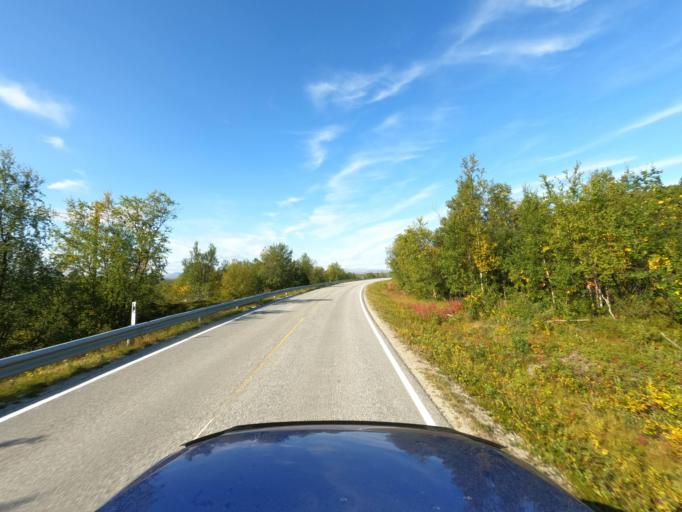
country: NO
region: Finnmark Fylke
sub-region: Porsanger
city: Lakselv
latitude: 69.7679
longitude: 25.1708
